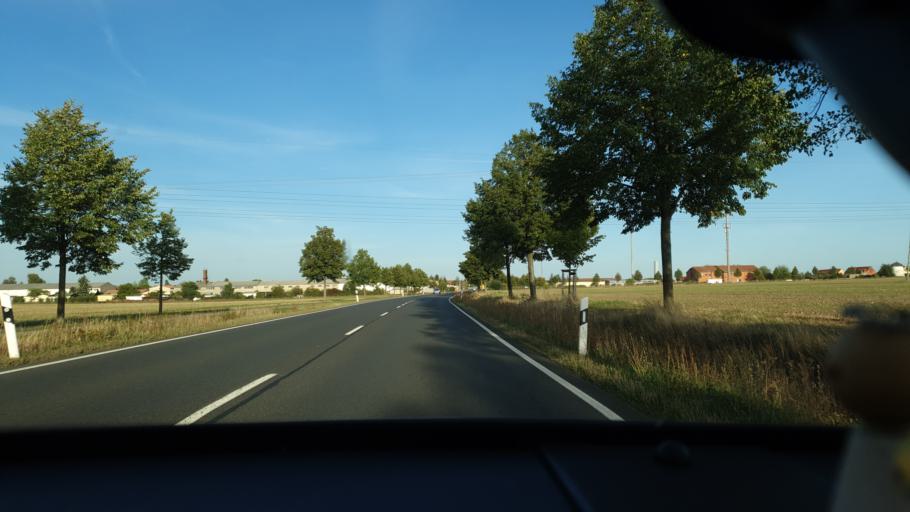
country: DE
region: Saxony
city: Eilenburg
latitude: 51.4589
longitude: 12.6025
